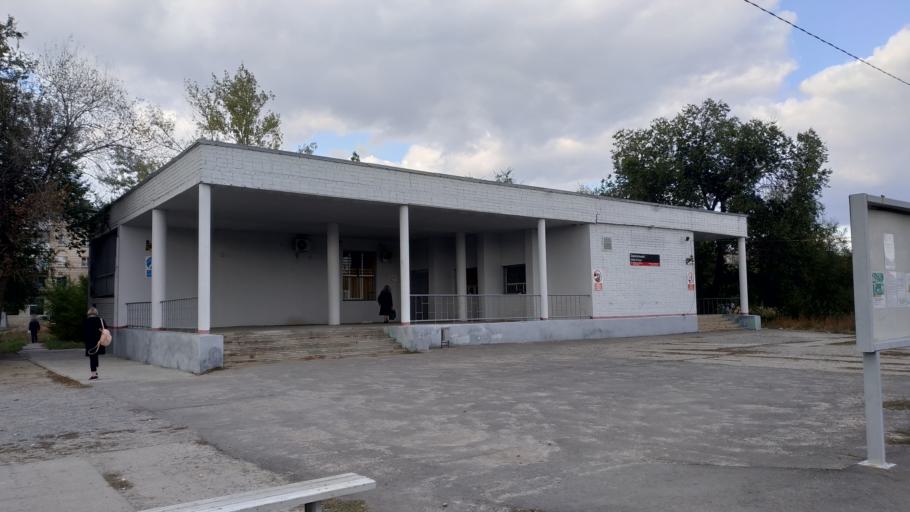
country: RU
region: Volgograd
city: Krasnoslobodsk
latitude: 48.5169
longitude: 44.5706
